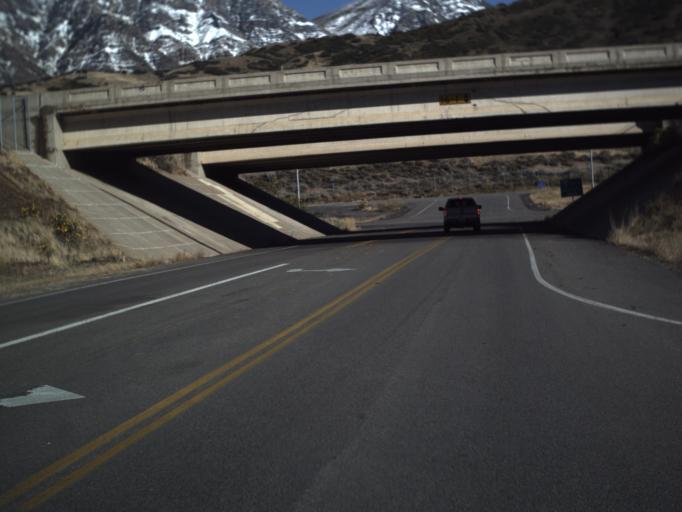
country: US
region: Utah
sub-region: Utah County
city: Santaquin
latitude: 39.9510
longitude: -111.8035
